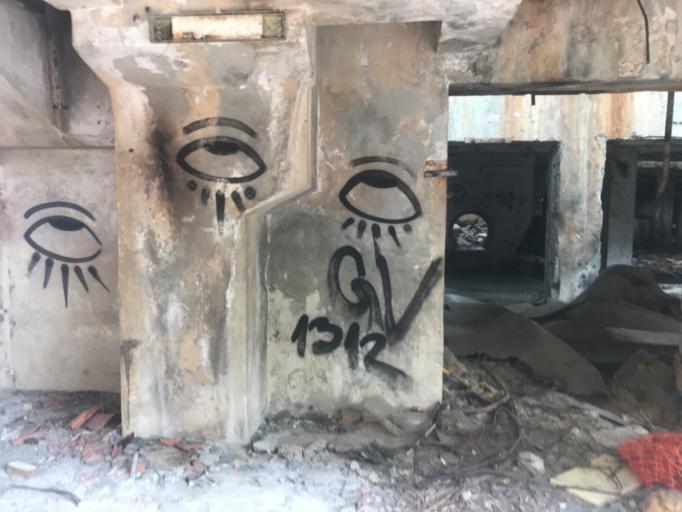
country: HR
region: Primorsko-Goranska
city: Drenova
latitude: 45.3331
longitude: 14.4524
